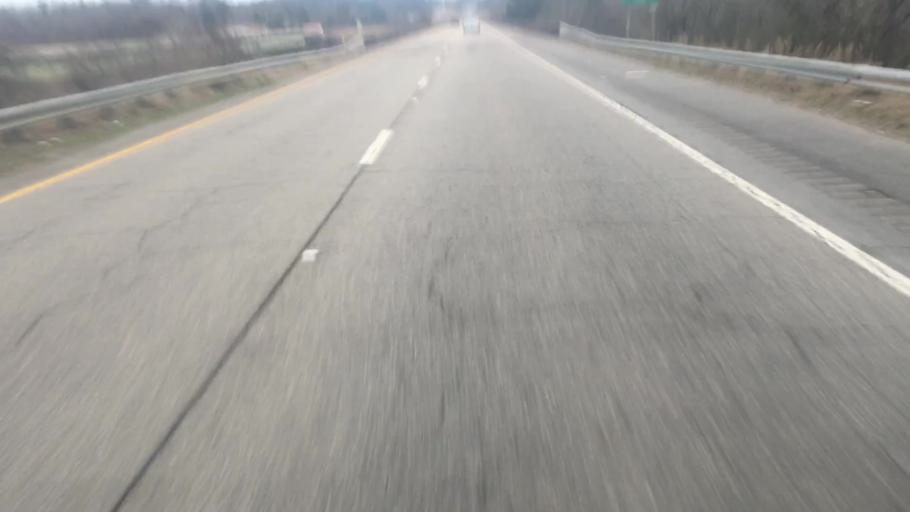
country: US
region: Alabama
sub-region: Walker County
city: Cordova
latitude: 33.8069
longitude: -87.1424
